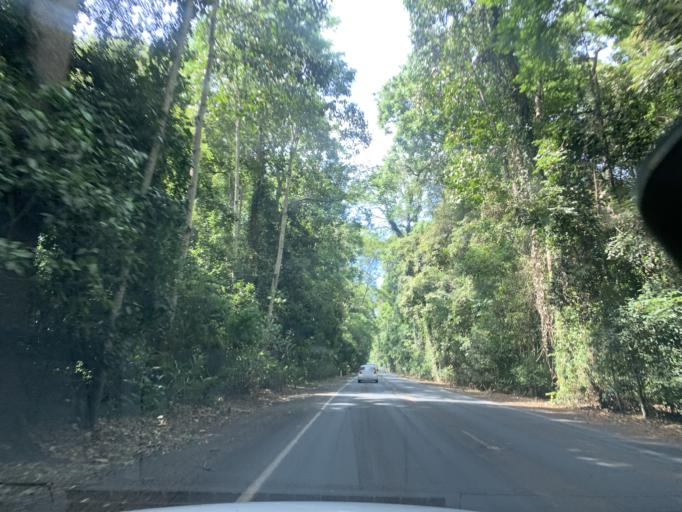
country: AU
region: Queensland
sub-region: Tablelands
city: Tolga
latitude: -17.2420
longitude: 145.4794
